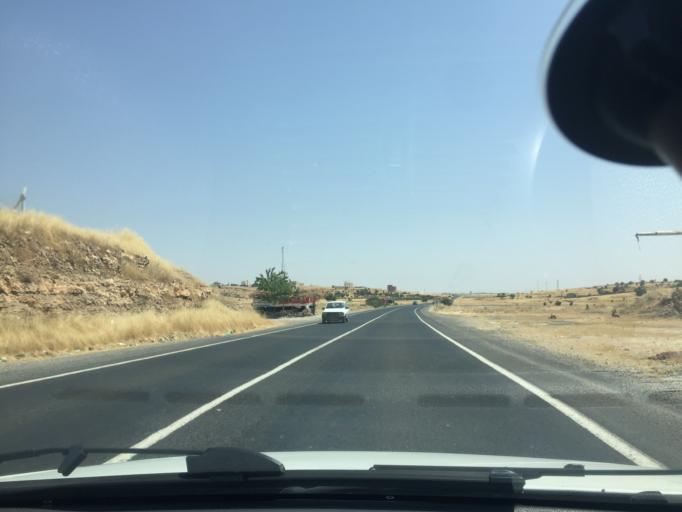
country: TR
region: Mardin
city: Acirli
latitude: 37.4465
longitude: 41.2800
